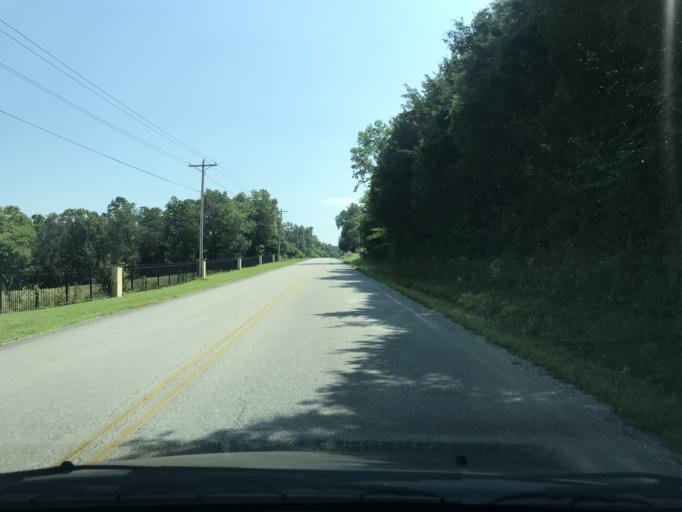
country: US
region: Tennessee
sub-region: Loudon County
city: Lenoir City
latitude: 35.8287
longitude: -84.3154
